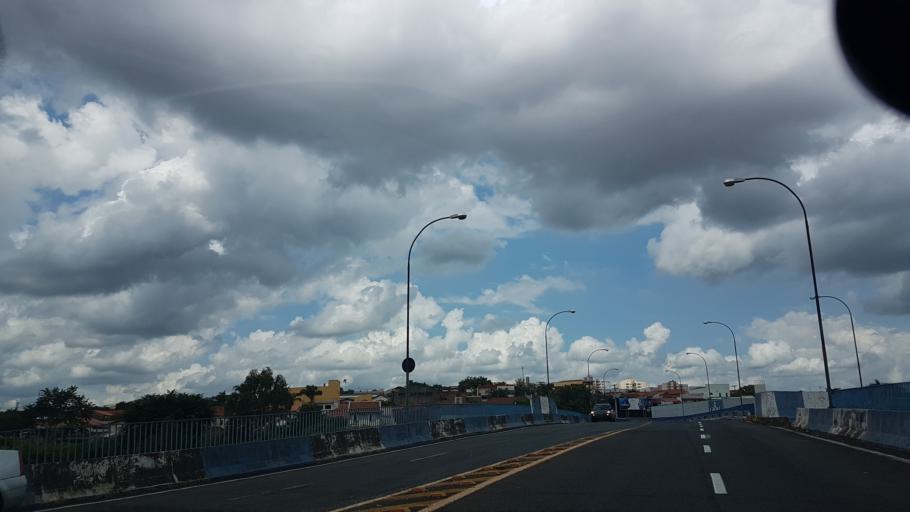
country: BR
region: Sao Paulo
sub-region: Limeira
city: Limeira
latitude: -22.5685
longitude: -47.3984
